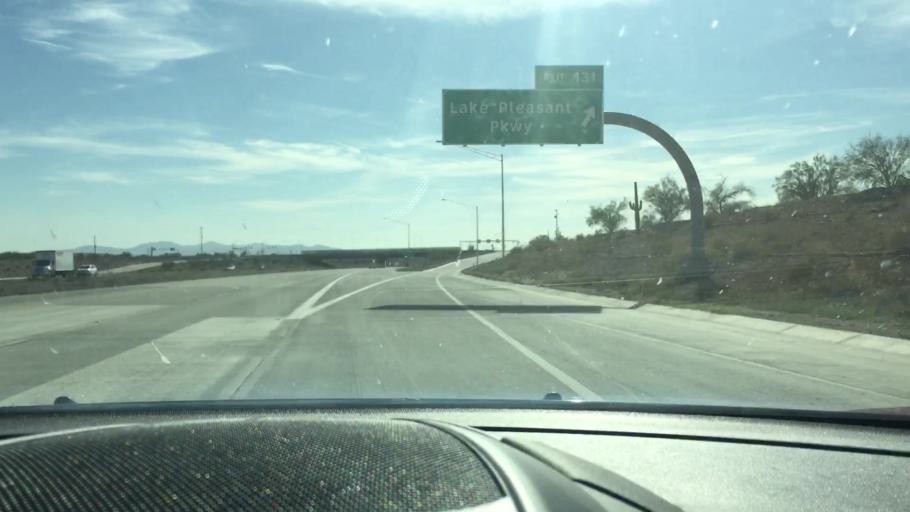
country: US
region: Arizona
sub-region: Maricopa County
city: Anthem
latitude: 33.7725
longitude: -112.2444
